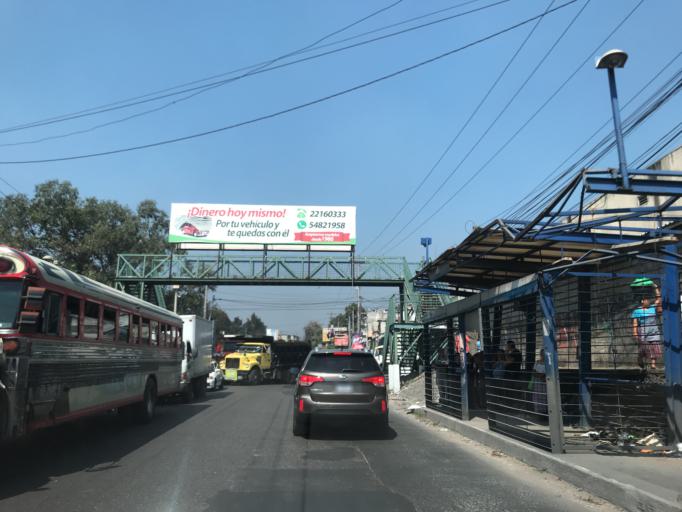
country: GT
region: Guatemala
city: Villa Nueva
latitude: 14.5393
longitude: -90.5566
